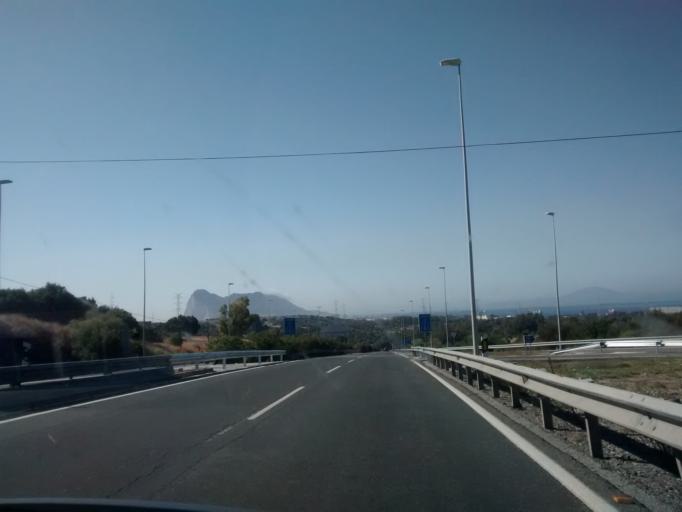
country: ES
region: Andalusia
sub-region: Provincia de Cadiz
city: San Roque
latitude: 36.2041
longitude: -5.3842
